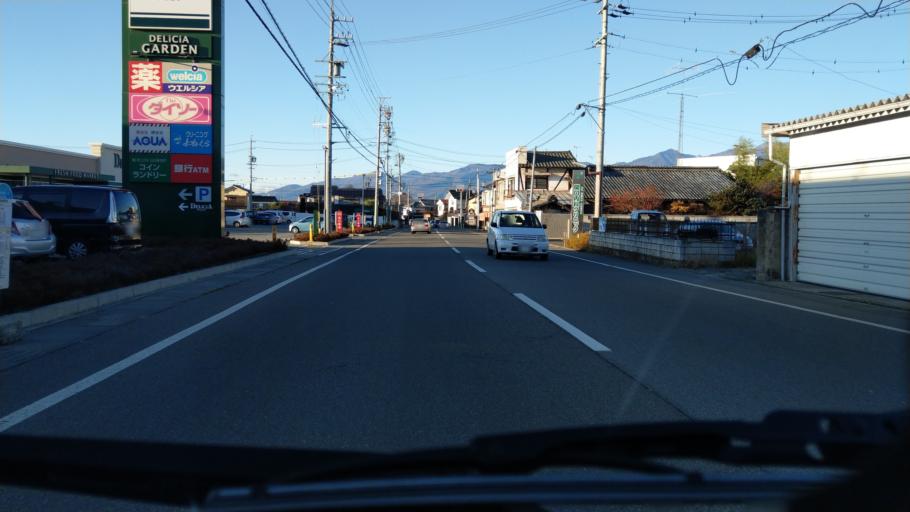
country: JP
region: Nagano
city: Saku
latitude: 36.2330
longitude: 138.4751
